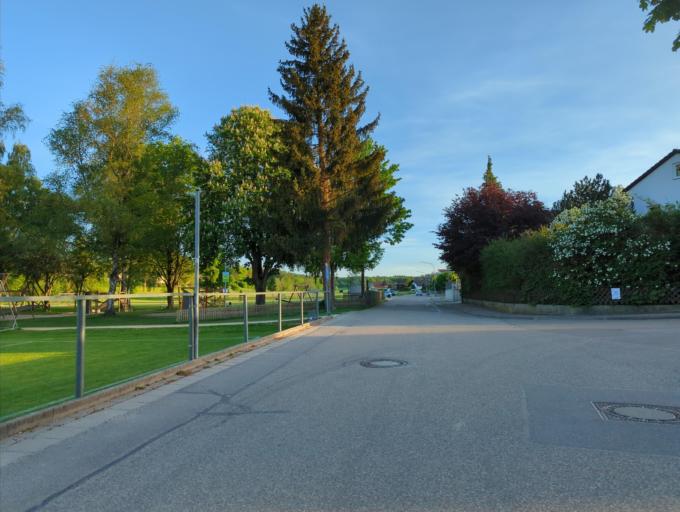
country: DE
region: Bavaria
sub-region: Upper Palatinate
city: Alteglofsheim
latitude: 48.9170
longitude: 12.2035
